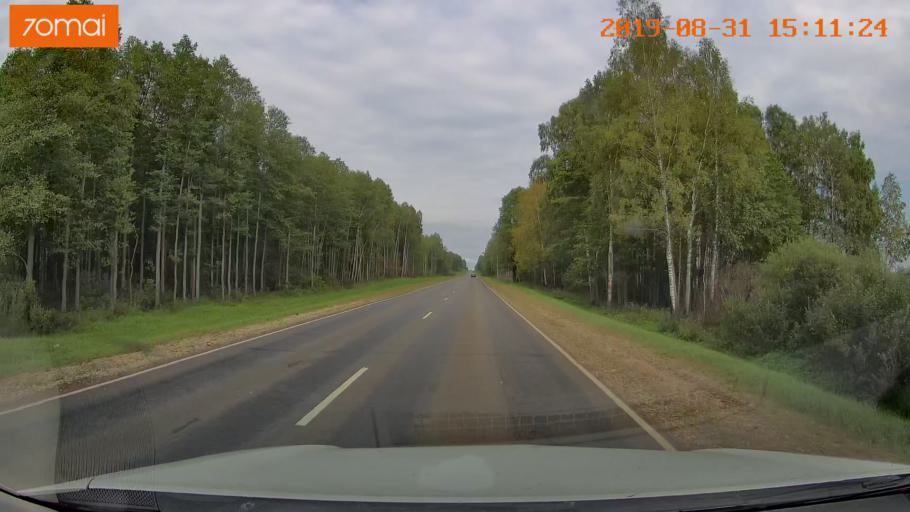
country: RU
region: Kaluga
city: Spas-Demensk
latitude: 54.4221
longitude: 34.2426
